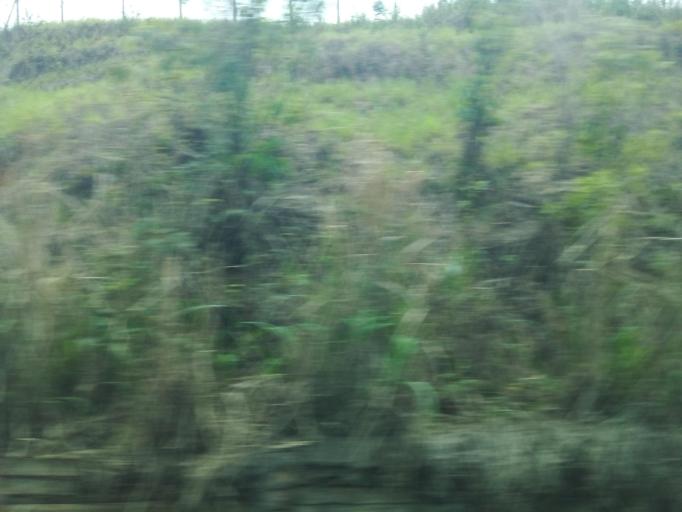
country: BR
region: Minas Gerais
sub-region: Ipatinga
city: Ipatinga
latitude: -19.4631
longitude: -42.4692
